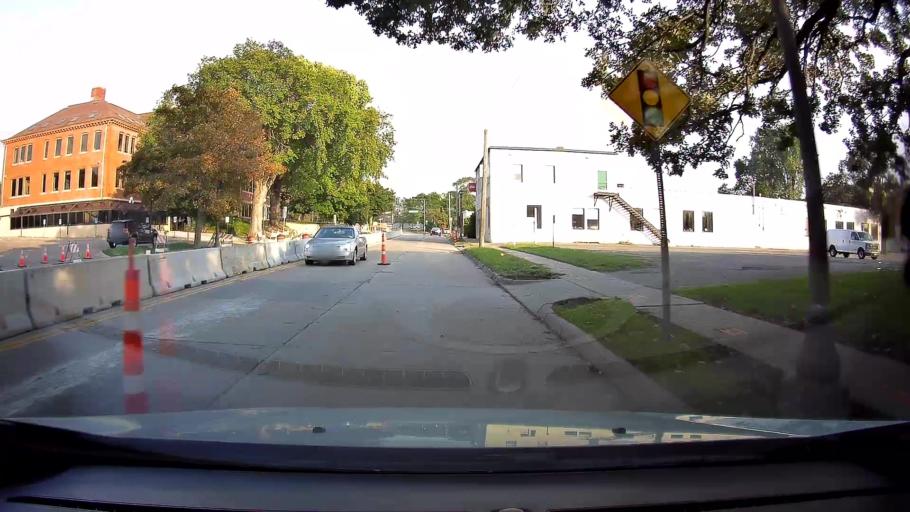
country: US
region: Minnesota
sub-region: Ramsey County
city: Lauderdale
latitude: 44.9660
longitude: -93.1989
